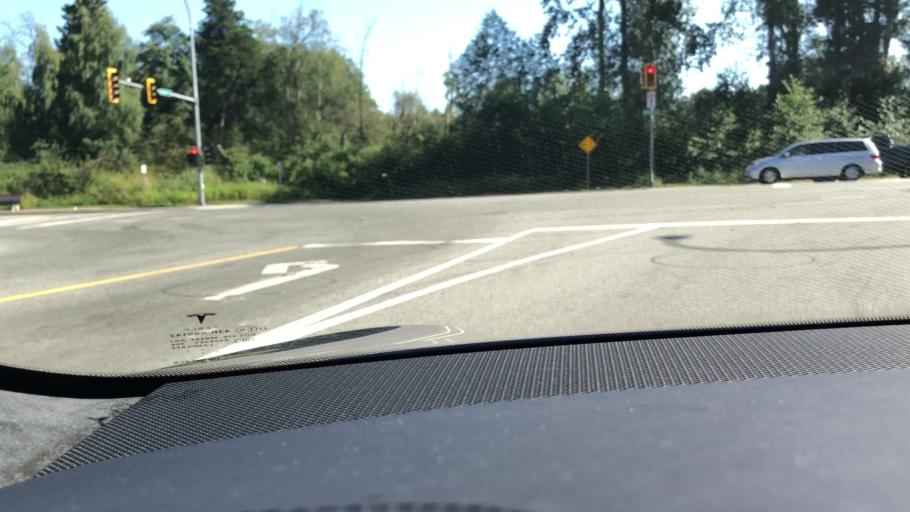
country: CA
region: British Columbia
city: Burnaby
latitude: 49.2503
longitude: -122.9710
